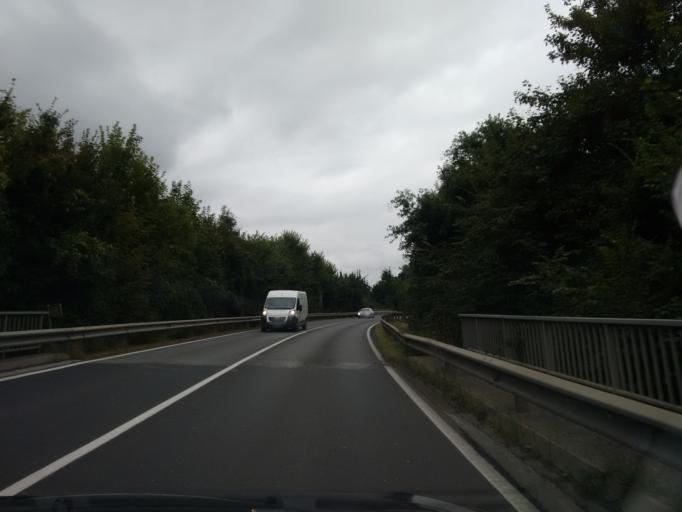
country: AT
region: Upper Austria
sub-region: Politischer Bezirk Grieskirchen
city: Bad Schallerbach
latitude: 48.2219
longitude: 13.9654
